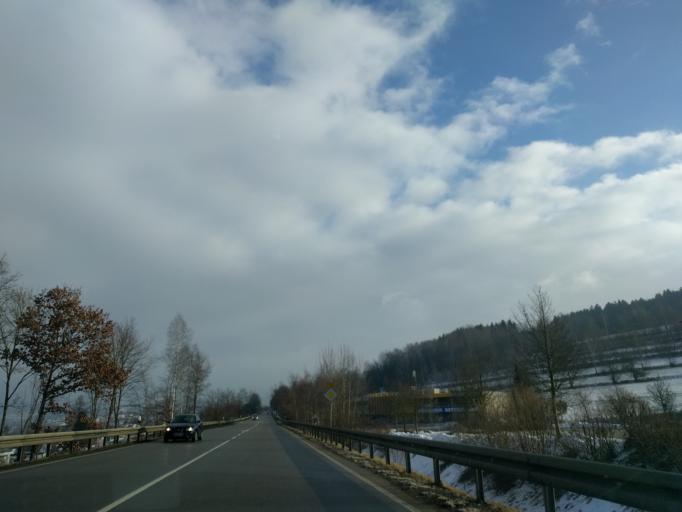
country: DE
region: Bavaria
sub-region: Lower Bavaria
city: Zwiesel
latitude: 49.0015
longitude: 13.2183
